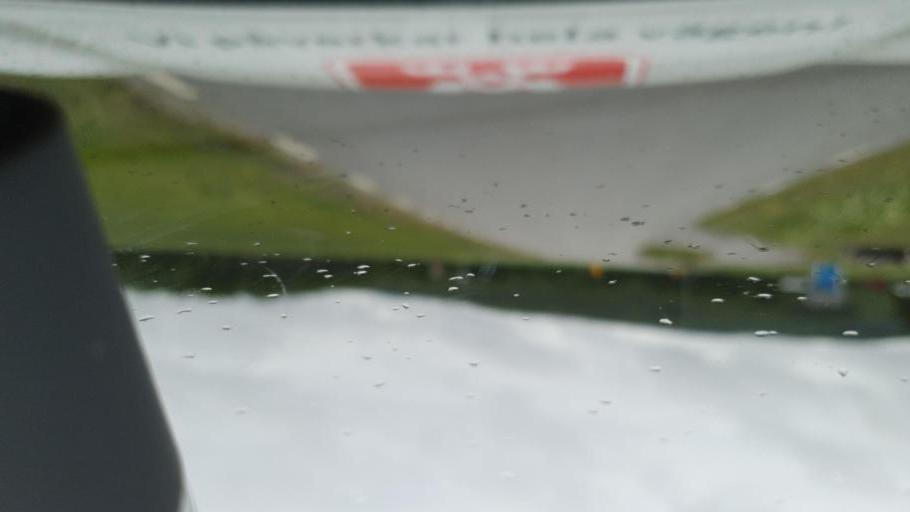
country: SE
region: Vaesterbotten
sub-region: Asele Kommun
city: Asele
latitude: 64.0104
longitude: 17.2593
